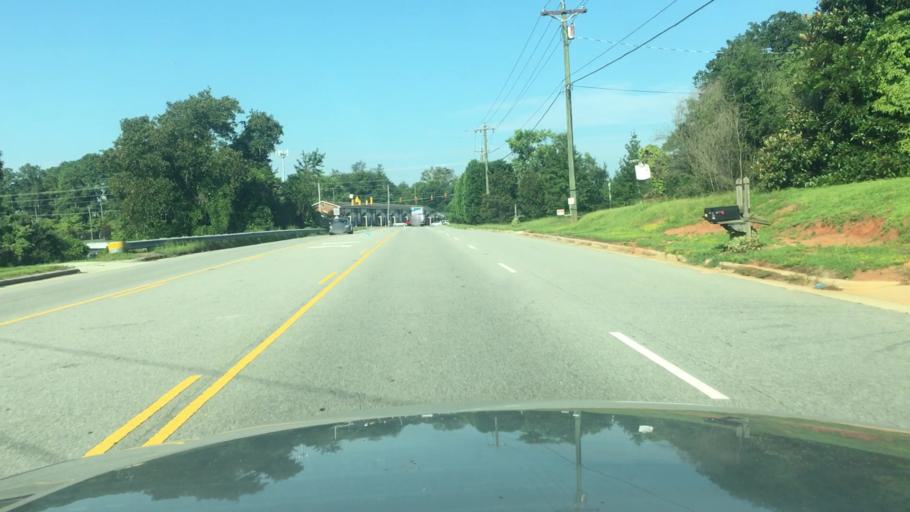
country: US
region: North Carolina
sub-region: Cumberland County
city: Spring Lake
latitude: 35.1540
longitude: -78.9106
